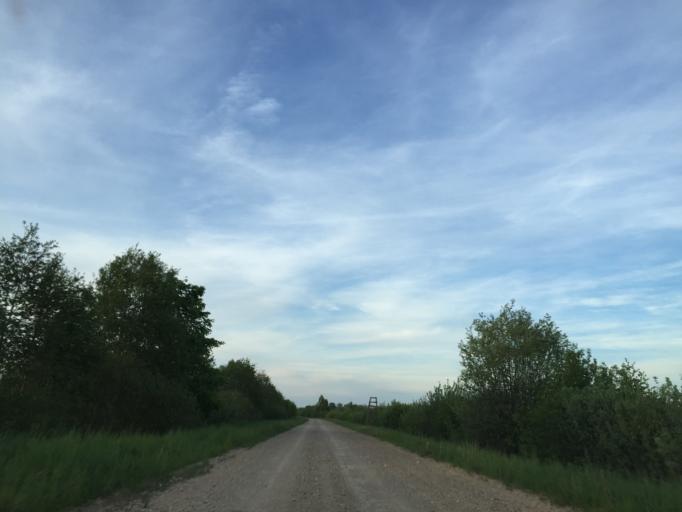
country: LV
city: Tireli
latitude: 56.7416
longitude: 23.5195
